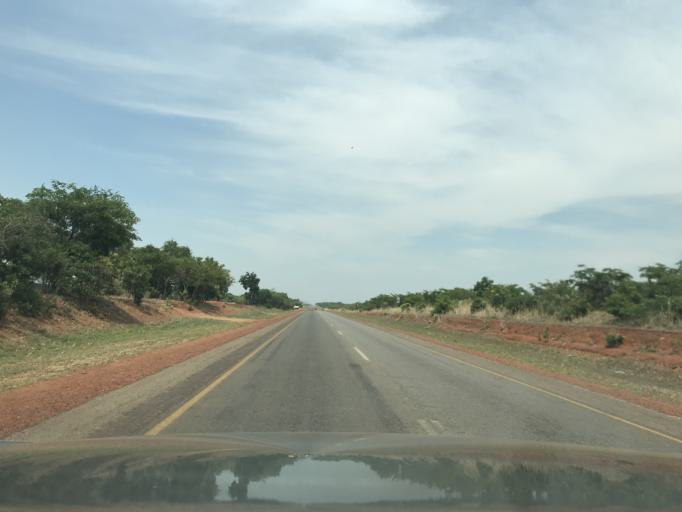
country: ZM
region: Northern
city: Kasama
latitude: -10.2208
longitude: 31.1313
